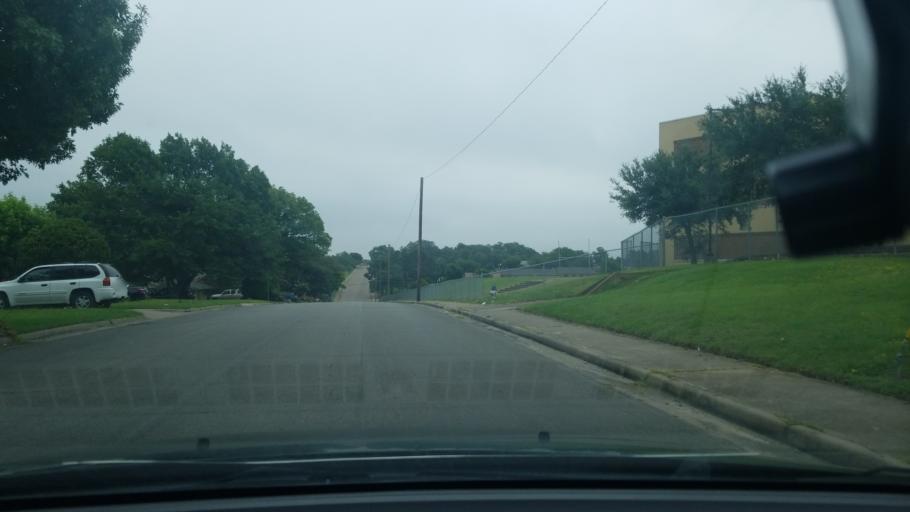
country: US
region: Texas
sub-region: Dallas County
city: Balch Springs
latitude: 32.7593
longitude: -96.6900
